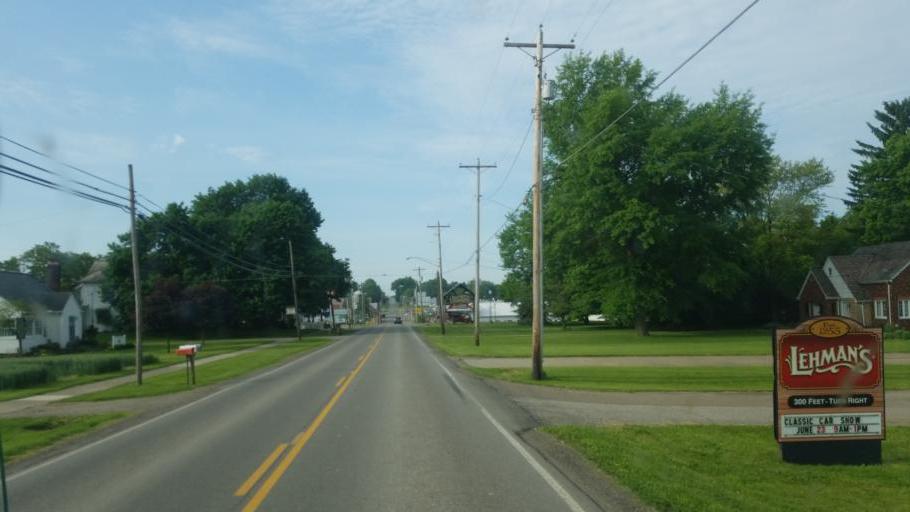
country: US
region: Ohio
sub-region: Wayne County
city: Dalton
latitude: 40.7435
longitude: -81.7452
